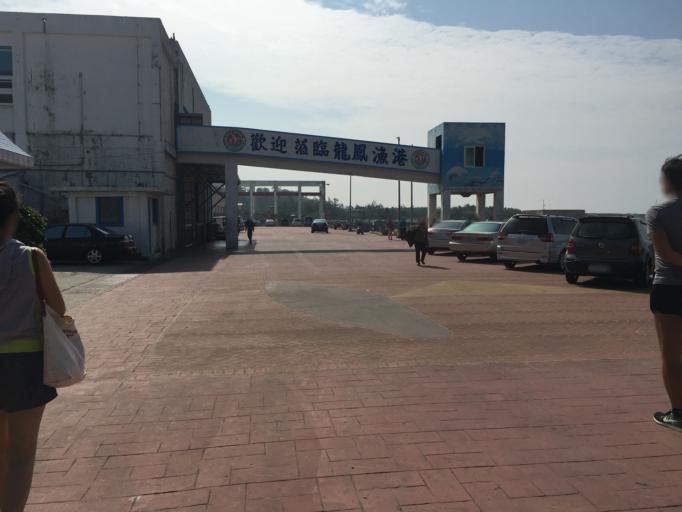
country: TW
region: Taiwan
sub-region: Miaoli
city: Miaoli
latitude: 24.7001
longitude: 120.8587
